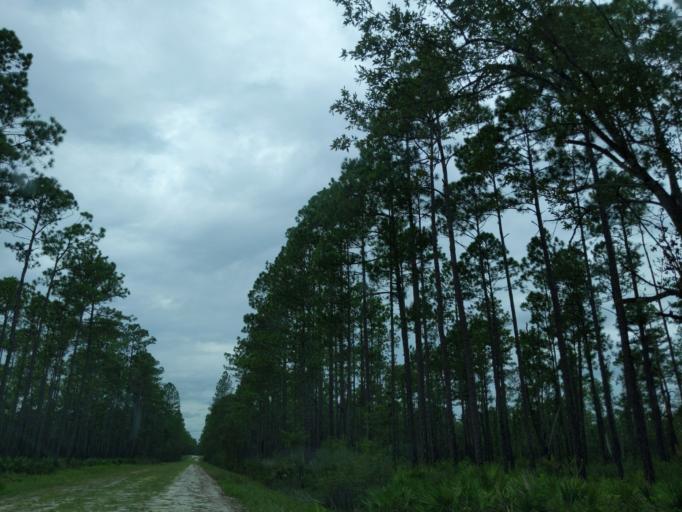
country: US
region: Florida
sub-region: Gadsden County
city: Midway
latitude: 30.3544
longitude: -84.5025
